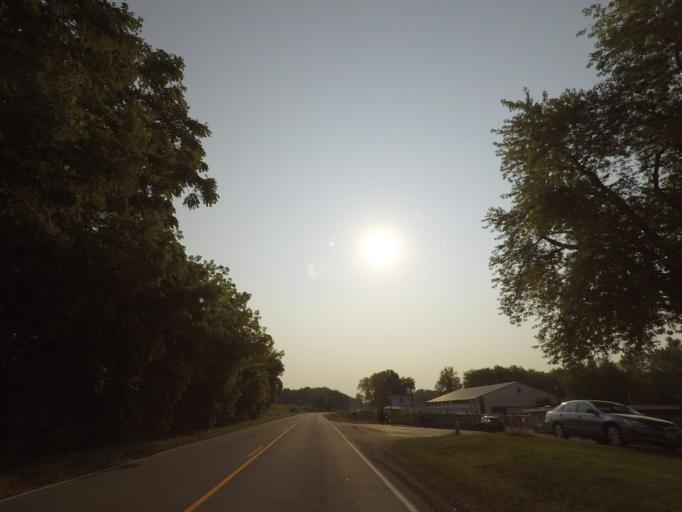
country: US
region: Wisconsin
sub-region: Dane County
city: McFarland
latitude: 43.0524
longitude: -89.2583
